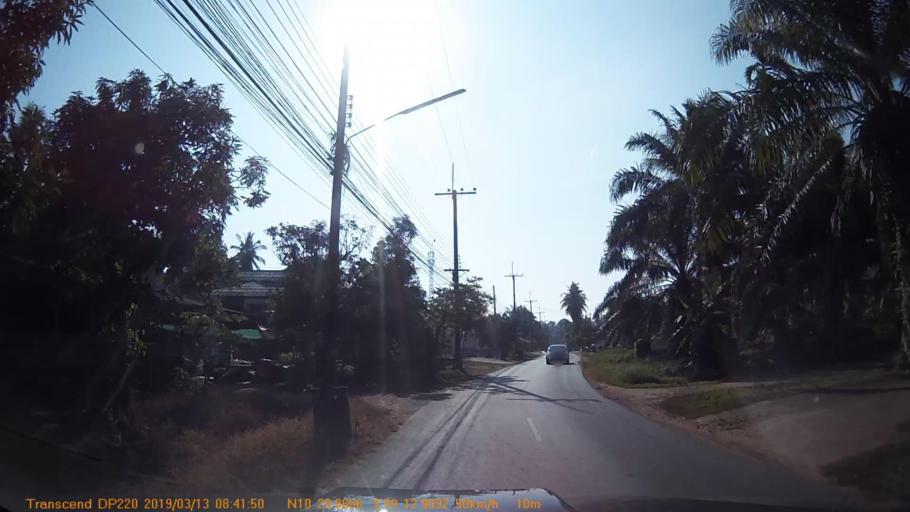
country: TH
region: Chumphon
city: Chumphon
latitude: 10.4977
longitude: 99.2153
